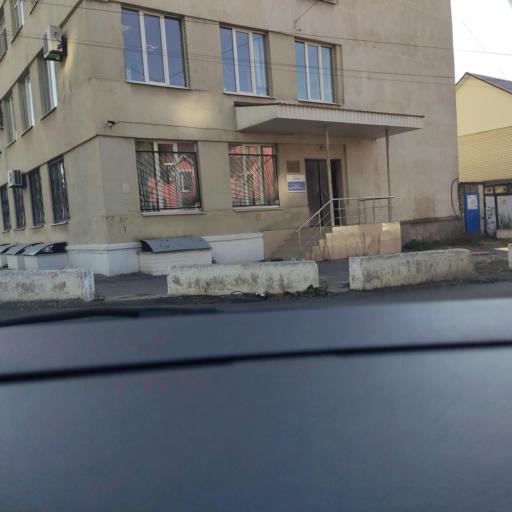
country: RU
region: Voronezj
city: Voronezh
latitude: 51.6824
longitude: 39.2135
